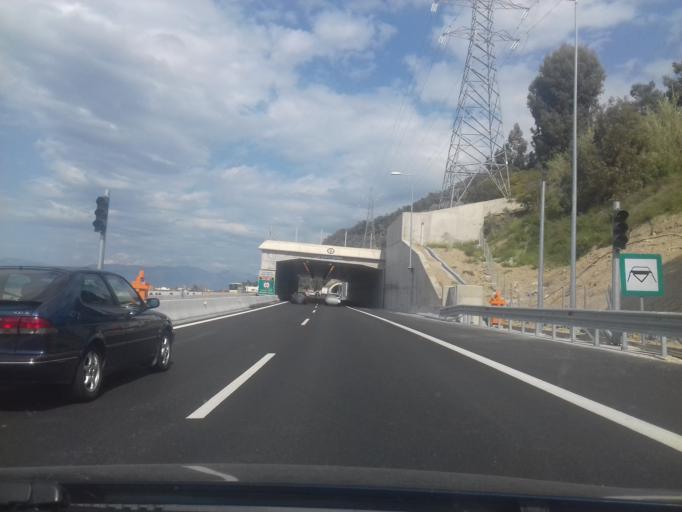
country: GR
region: West Greece
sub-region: Nomos Achaias
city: Aiyira
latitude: 38.1292
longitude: 22.4162
